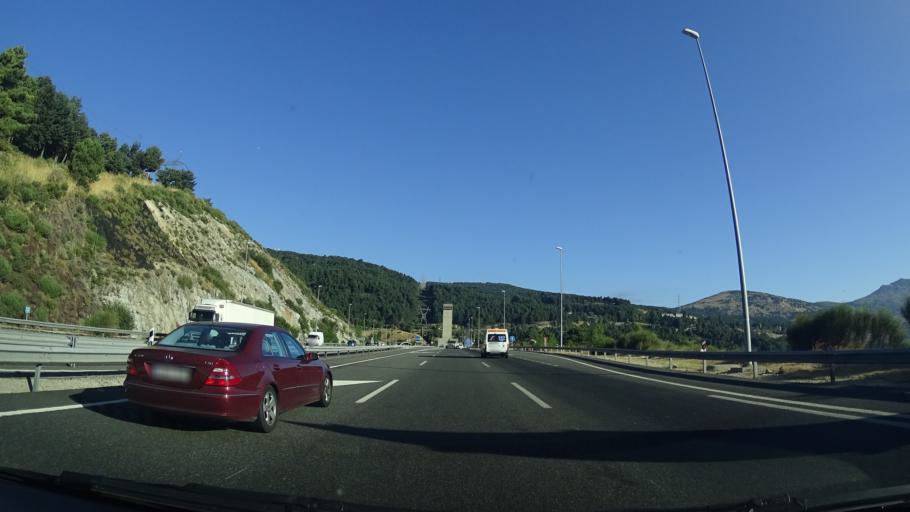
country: ES
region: Madrid
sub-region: Provincia de Madrid
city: Guadarrama
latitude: 40.6953
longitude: -4.1254
